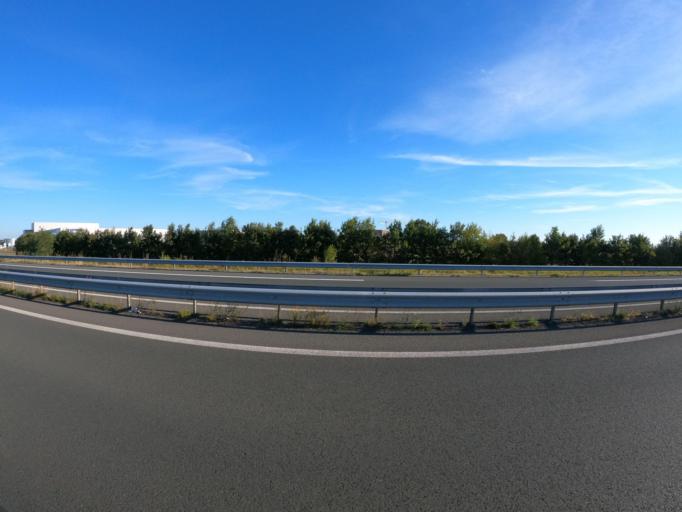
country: FR
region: Pays de la Loire
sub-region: Departement de Maine-et-Loire
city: Chemille-Melay
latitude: 47.2375
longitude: -0.7383
